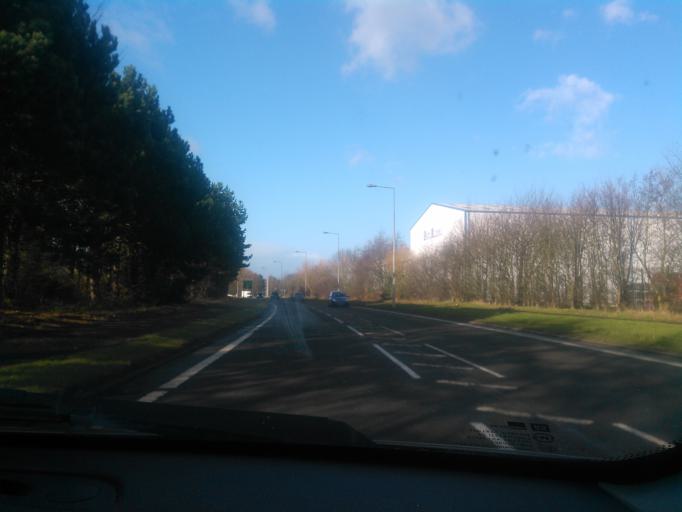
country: GB
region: England
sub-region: Shropshire
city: Hadley
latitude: 52.7150
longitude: -2.4723
